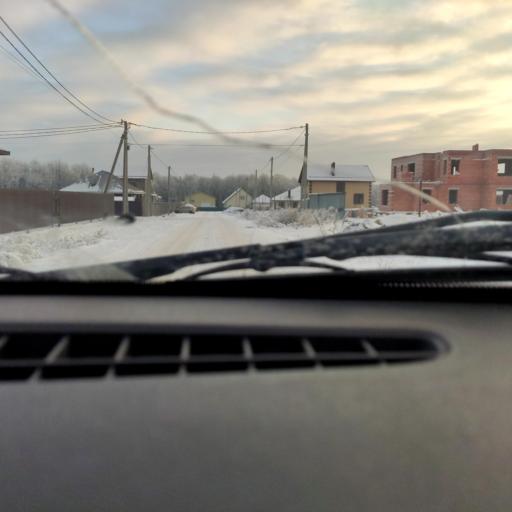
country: RU
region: Bashkortostan
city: Mikhaylovka
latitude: 54.8272
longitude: 55.8884
